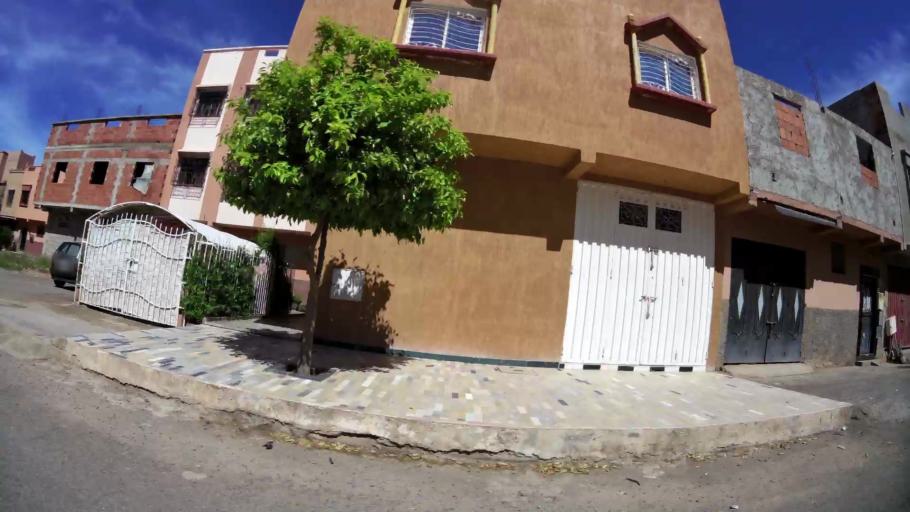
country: MA
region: Marrakech-Tensift-Al Haouz
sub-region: Marrakech
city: Marrakesh
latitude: 31.6378
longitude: -8.1092
